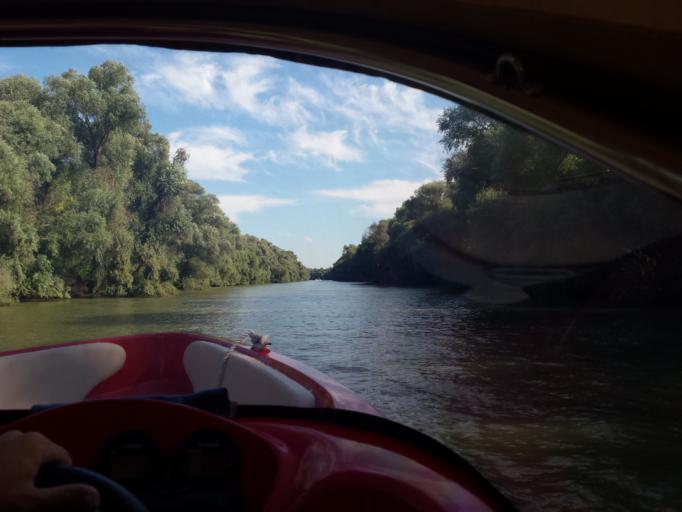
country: RO
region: Tulcea
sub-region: Comuna Pardina
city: Pardina
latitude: 45.2435
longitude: 28.9211
